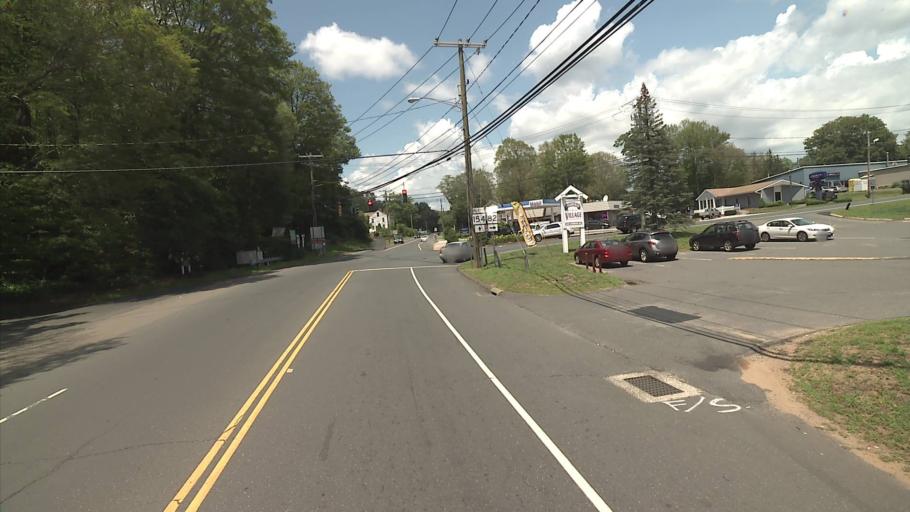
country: US
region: Connecticut
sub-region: Middlesex County
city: East Haddam
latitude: 41.4475
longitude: -72.4752
